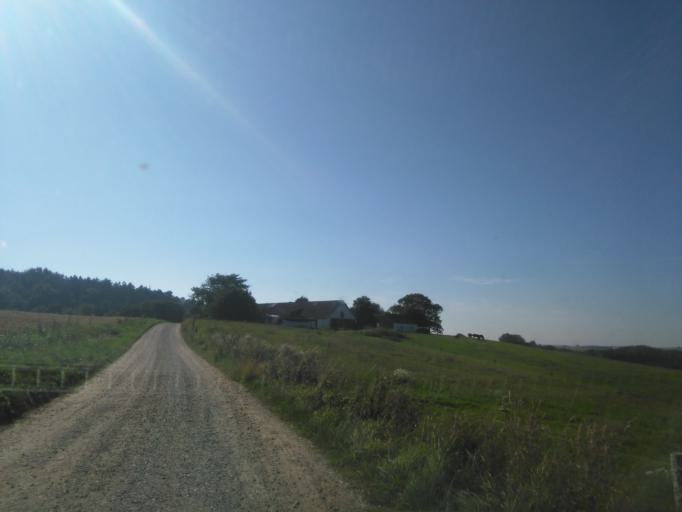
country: DK
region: Central Jutland
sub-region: Syddjurs Kommune
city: Ronde
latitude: 56.1996
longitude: 10.5193
